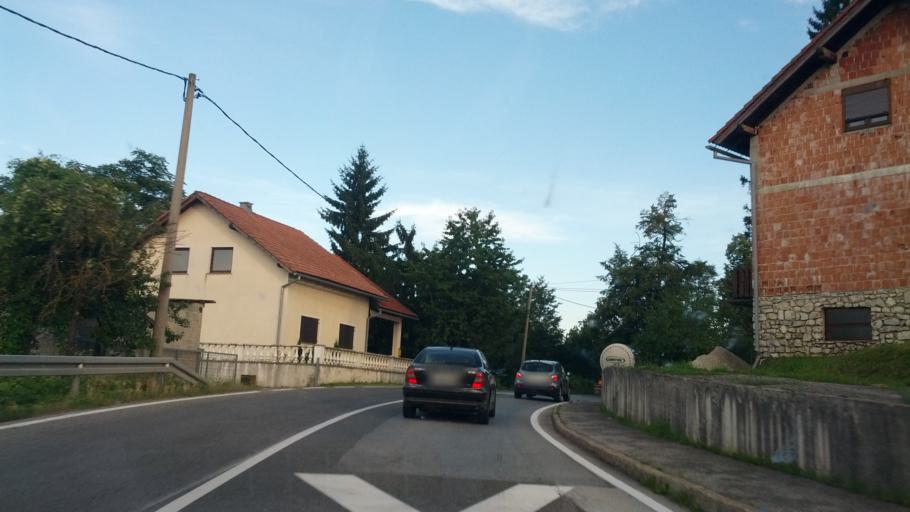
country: HR
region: Licko-Senjska
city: Jezerce
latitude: 44.9506
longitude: 15.6736
